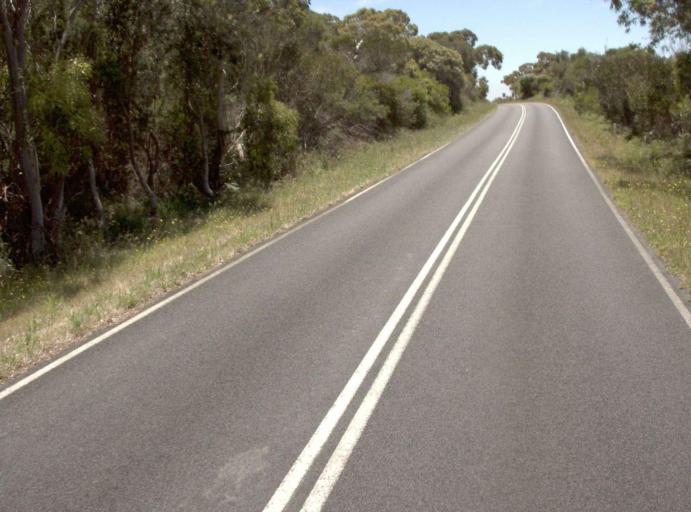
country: AU
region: Victoria
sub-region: Latrobe
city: Morwell
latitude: -38.8524
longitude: 146.2449
